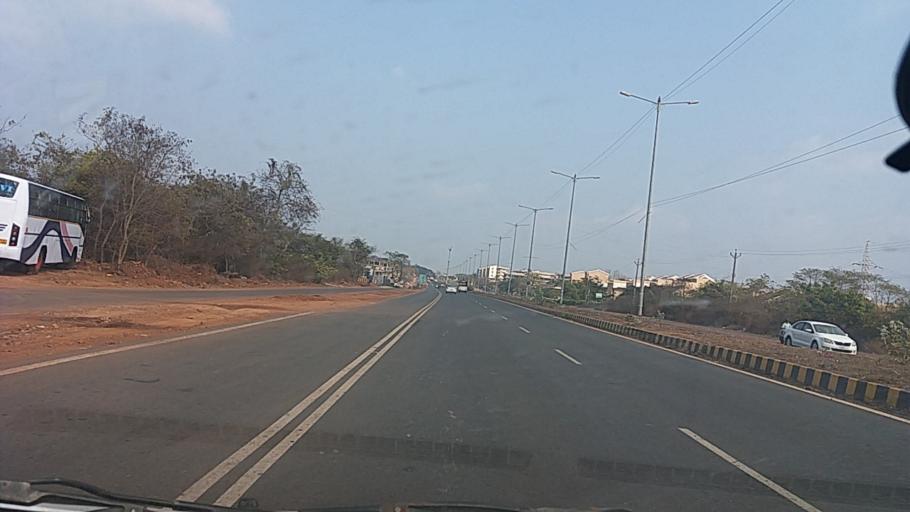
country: IN
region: Goa
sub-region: North Goa
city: Bambolim
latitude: 15.4923
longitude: 73.8872
